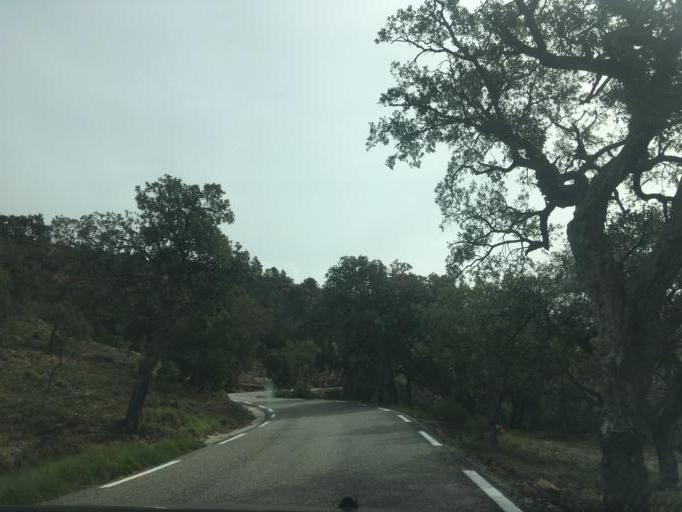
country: FR
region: Provence-Alpes-Cote d'Azur
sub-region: Departement du Var
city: Bagnols-en-Foret
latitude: 43.5163
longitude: 6.6419
